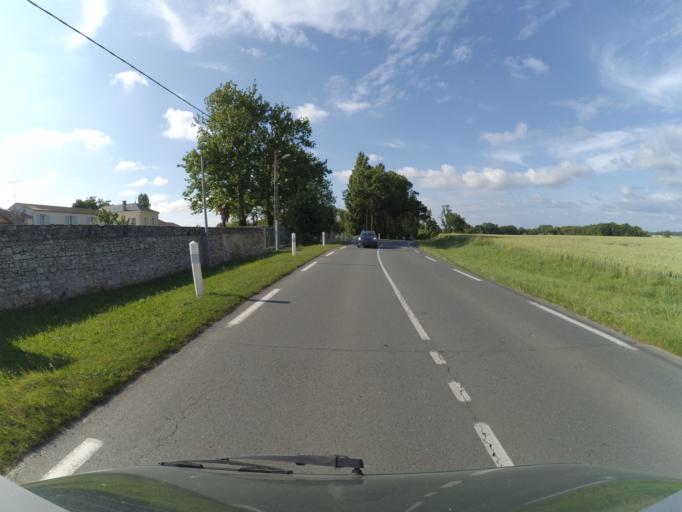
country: FR
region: Poitou-Charentes
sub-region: Departement de la Charente-Maritime
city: Le Gua
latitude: 45.7457
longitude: -0.9493
